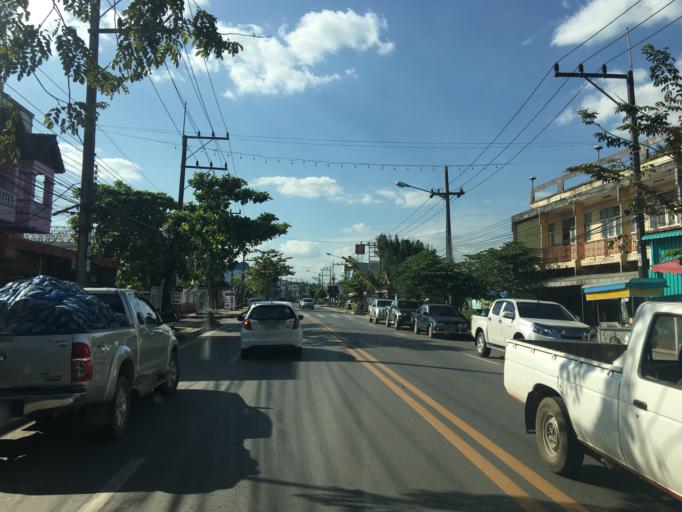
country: TH
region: Phayao
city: Chun
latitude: 19.3411
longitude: 100.1242
